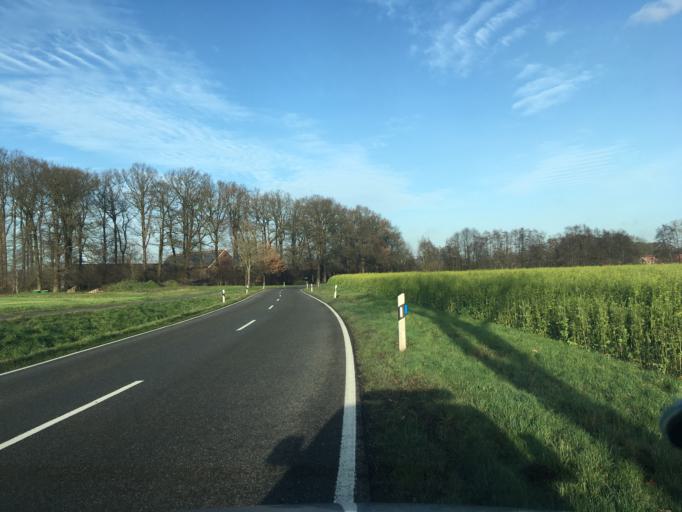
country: DE
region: North Rhine-Westphalia
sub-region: Regierungsbezirk Munster
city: Gescher
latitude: 51.9418
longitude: 7.0472
